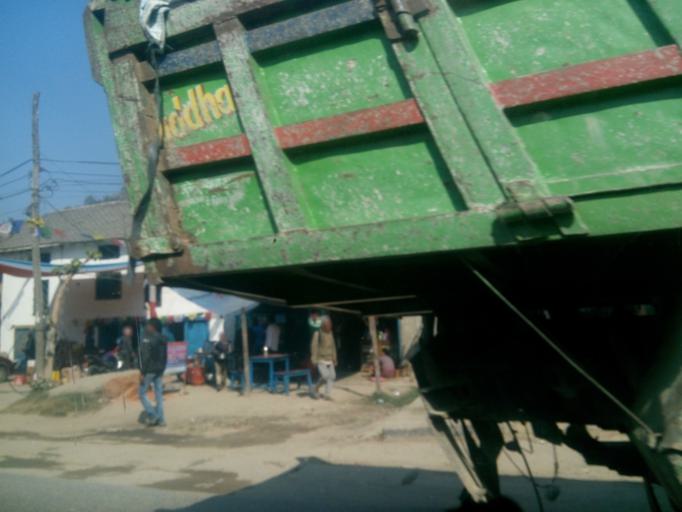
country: NP
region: Central Region
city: Kirtipur
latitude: 27.7517
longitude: 85.0668
